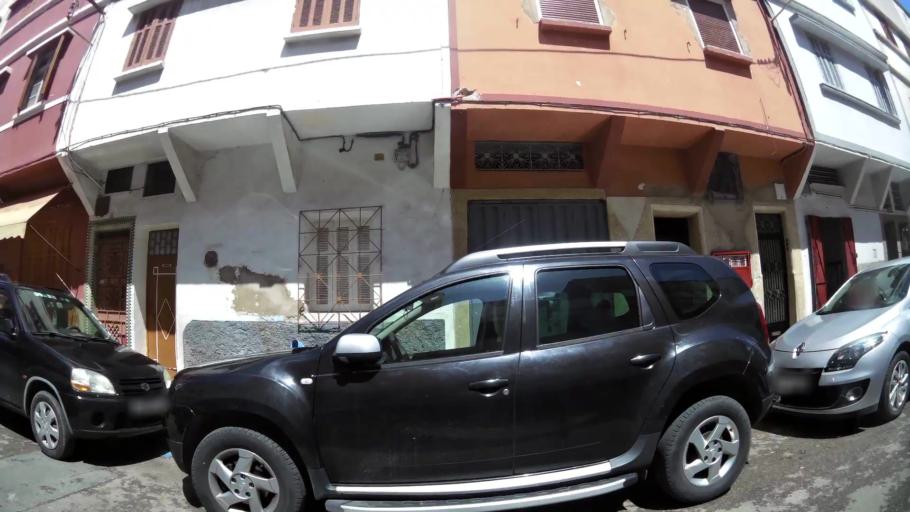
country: MA
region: Grand Casablanca
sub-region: Casablanca
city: Casablanca
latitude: 33.5605
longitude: -7.5983
